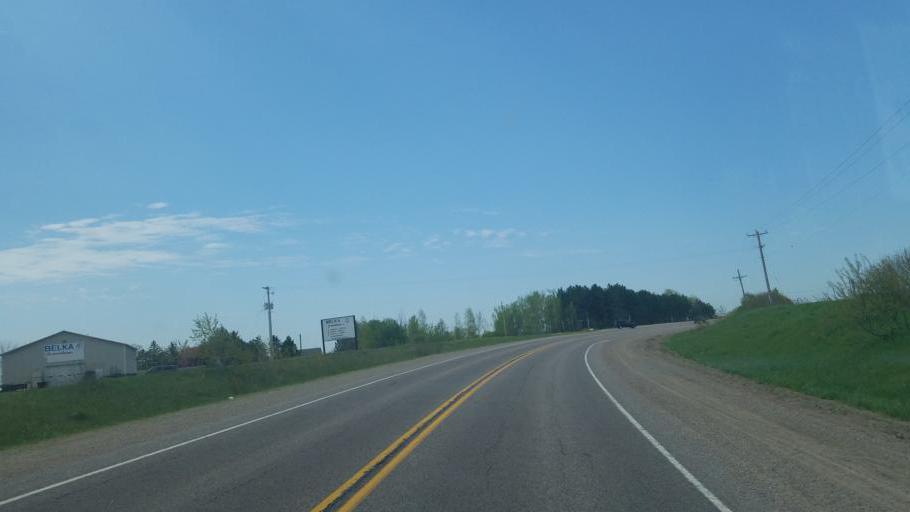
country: US
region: Wisconsin
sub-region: Marathon County
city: Spencer
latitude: 44.5853
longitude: -90.3768
